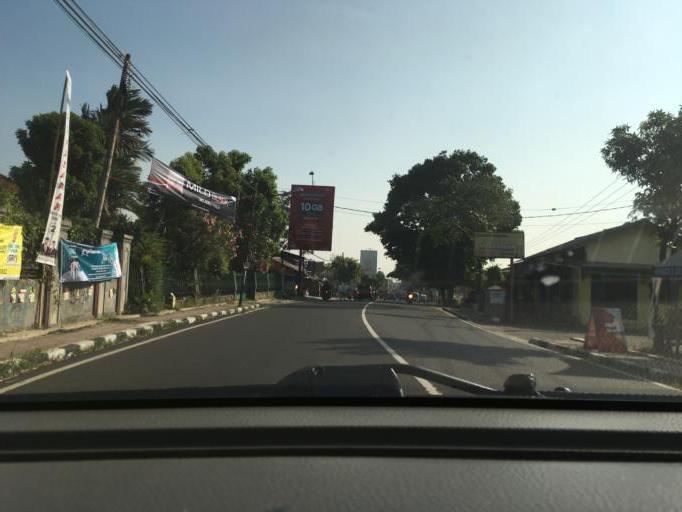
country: ID
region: West Java
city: Kuningan
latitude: -6.9188
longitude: 108.4871
